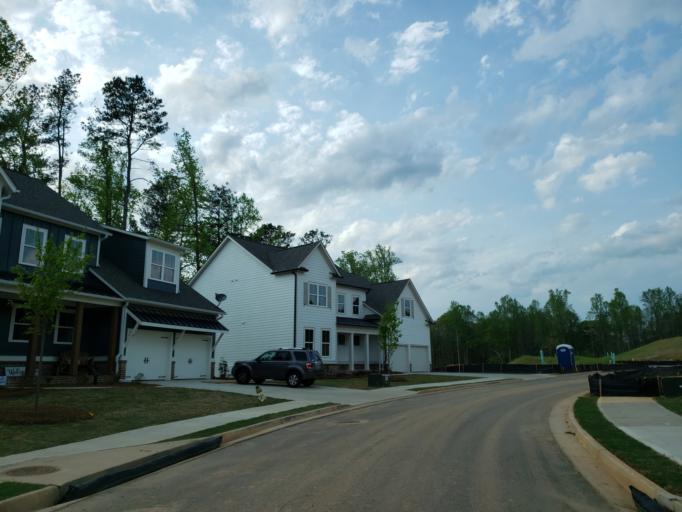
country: US
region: Georgia
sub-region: Cherokee County
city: Holly Springs
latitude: 34.1716
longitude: -84.4333
